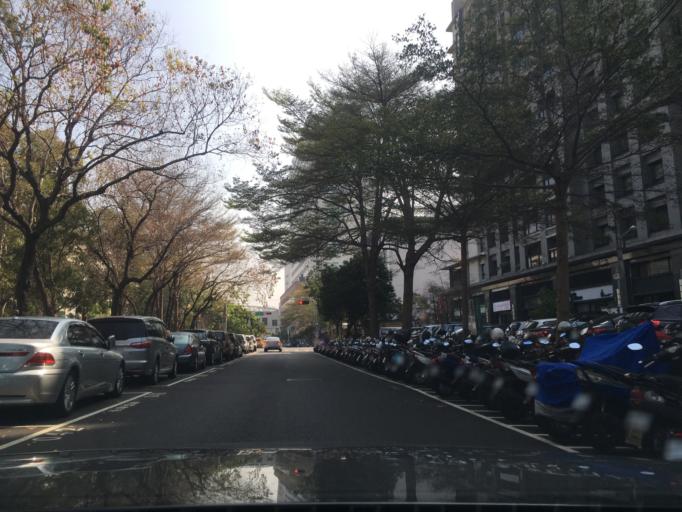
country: TW
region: Taiwan
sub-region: Taichung City
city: Taichung
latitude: 24.1573
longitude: 120.6780
